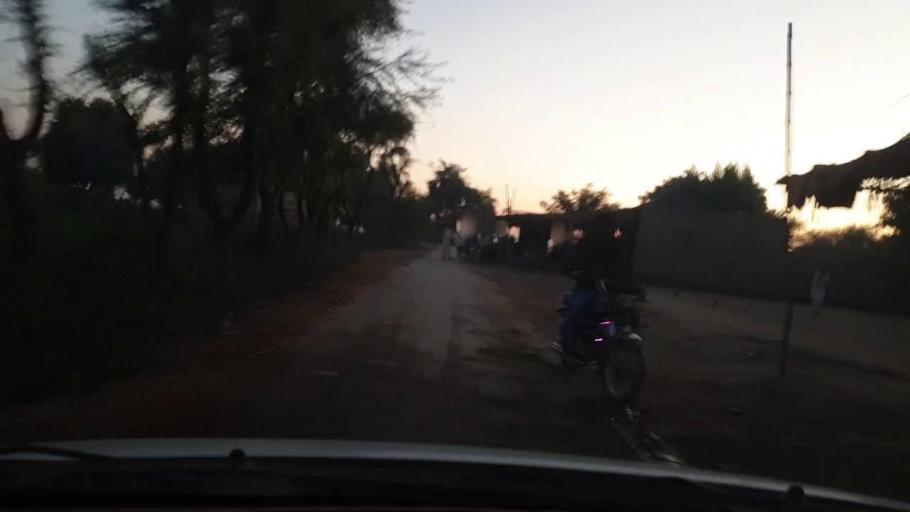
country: PK
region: Sindh
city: Khairpur Nathan Shah
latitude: 27.1384
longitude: 67.7177
